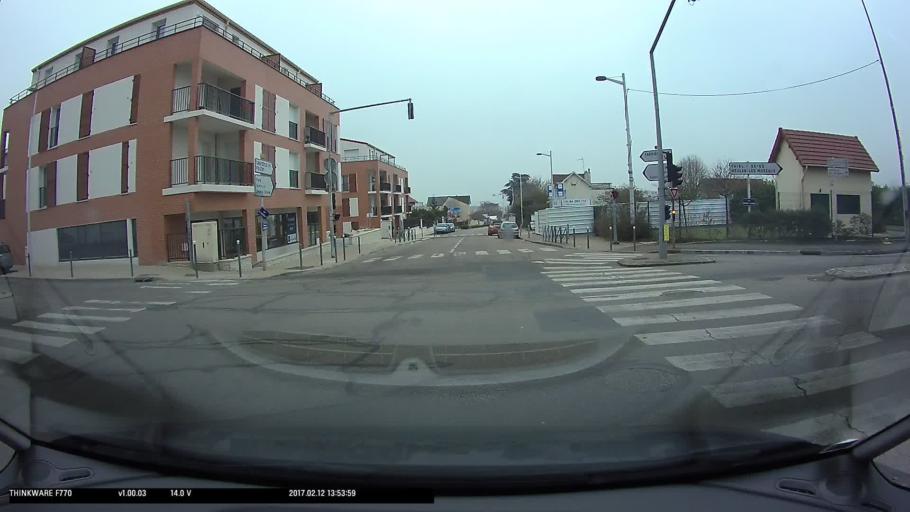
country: FR
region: Ile-de-France
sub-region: Departement des Yvelines
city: Chanteloup-les-Vignes
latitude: 48.9754
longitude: 2.0318
